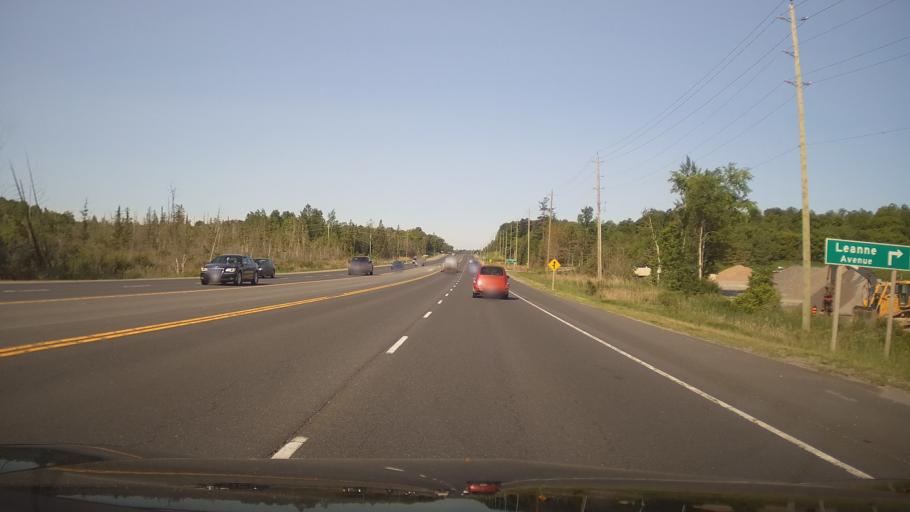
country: CA
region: Ontario
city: Peterborough
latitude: 44.3150
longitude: -78.2123
